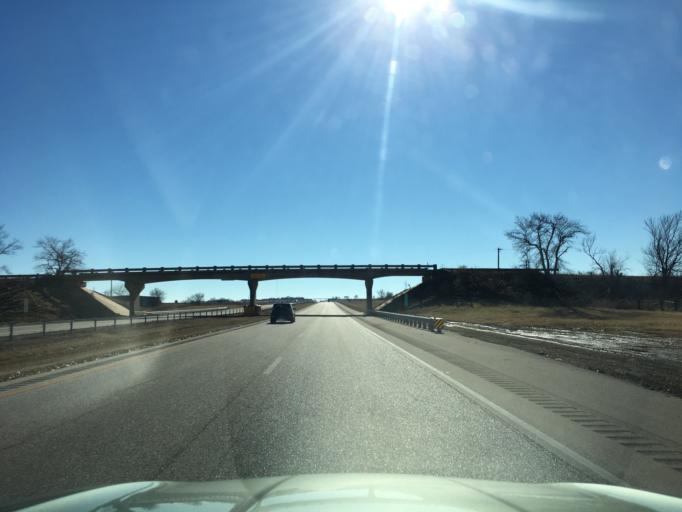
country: US
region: Oklahoma
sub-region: Kay County
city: Blackwell
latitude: 36.8849
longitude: -97.3522
